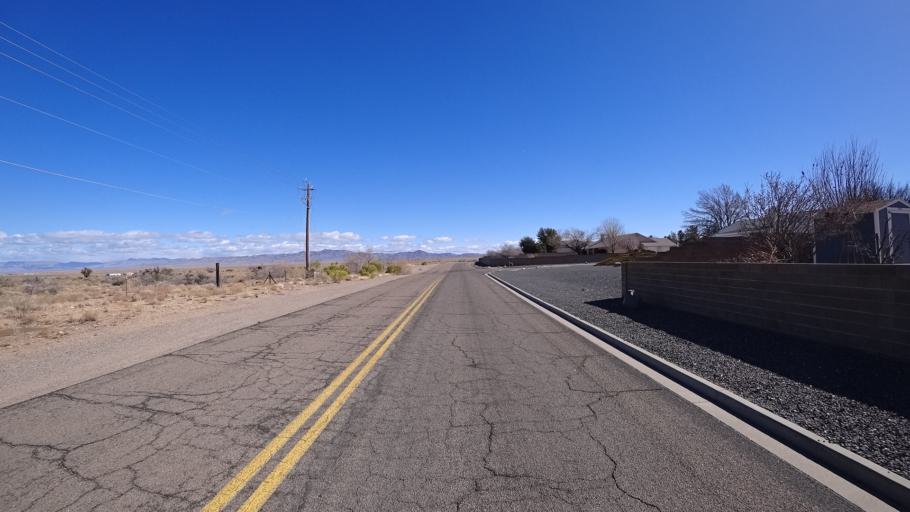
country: US
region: Arizona
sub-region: Mohave County
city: Kingman
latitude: 35.2040
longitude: -113.9662
